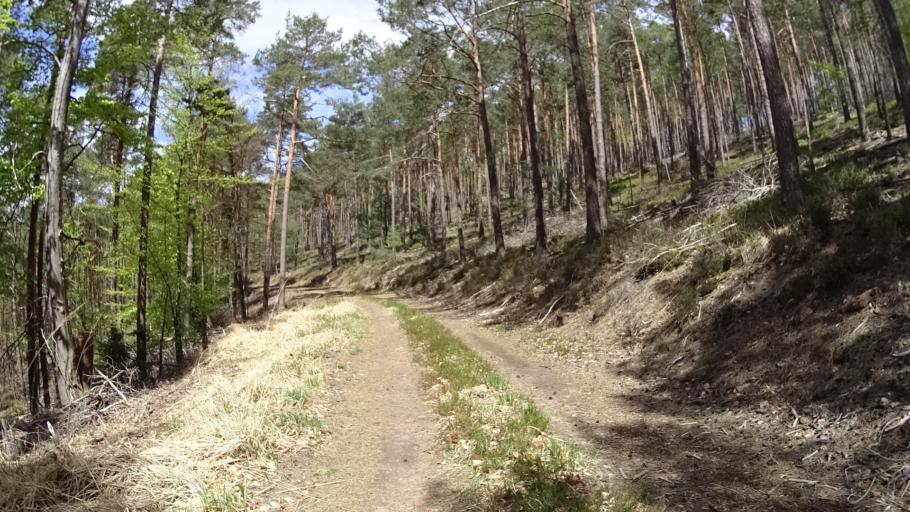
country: DE
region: Rheinland-Pfalz
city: Ramberg
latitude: 49.3086
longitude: 8.0050
